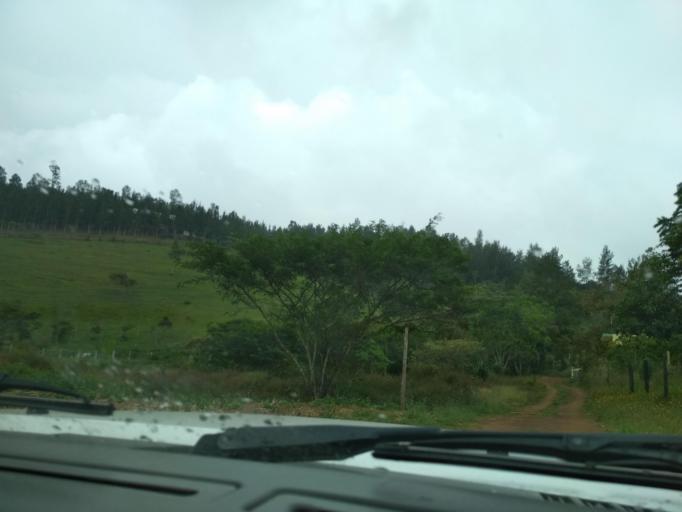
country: MX
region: Veracruz
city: El Castillo
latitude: 19.5377
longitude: -96.8329
